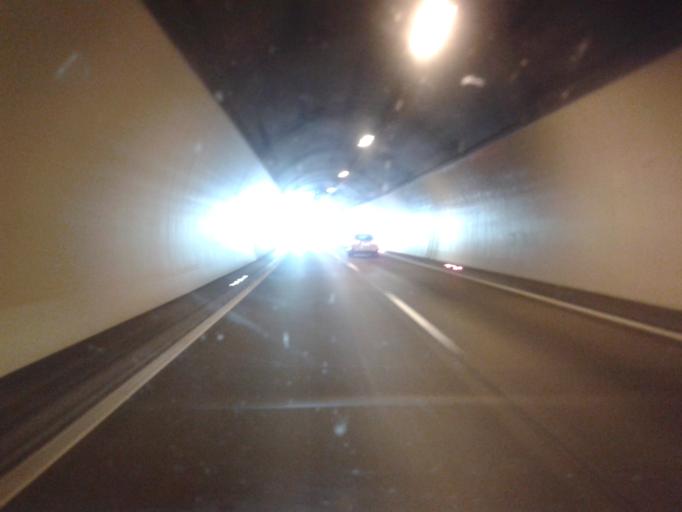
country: AT
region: Carinthia
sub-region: Politischer Bezirk Wolfsberg
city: Wolfsberg
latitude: 46.9014
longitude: 14.8213
